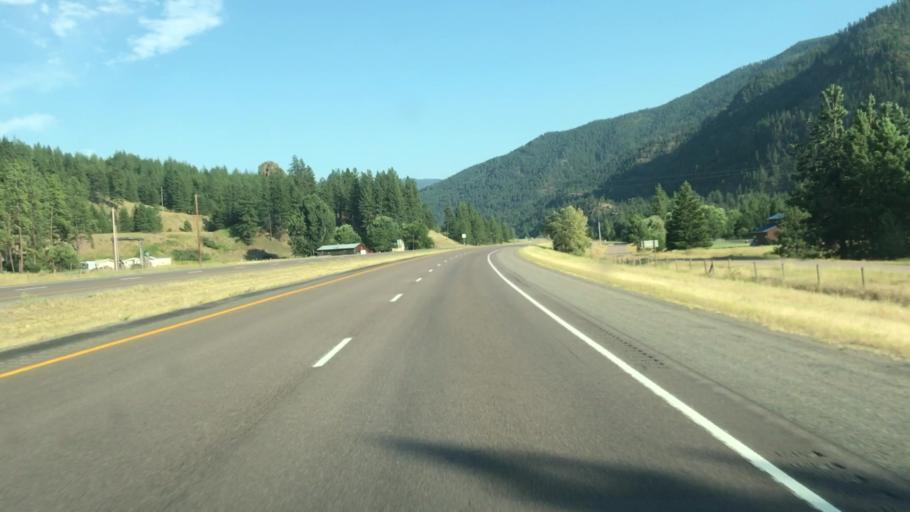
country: US
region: Montana
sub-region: Missoula County
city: Frenchtown
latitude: 47.0146
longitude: -114.5049
